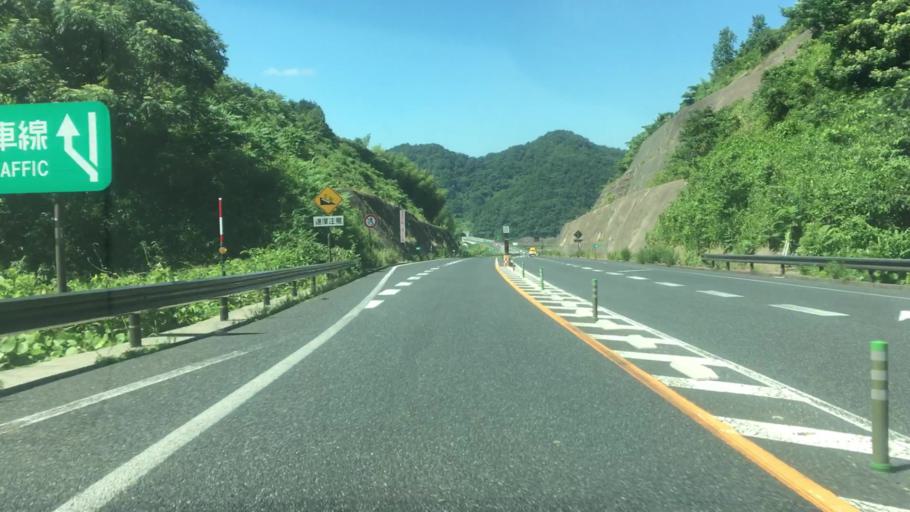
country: JP
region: Tottori
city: Tottori
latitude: 35.3698
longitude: 134.2029
